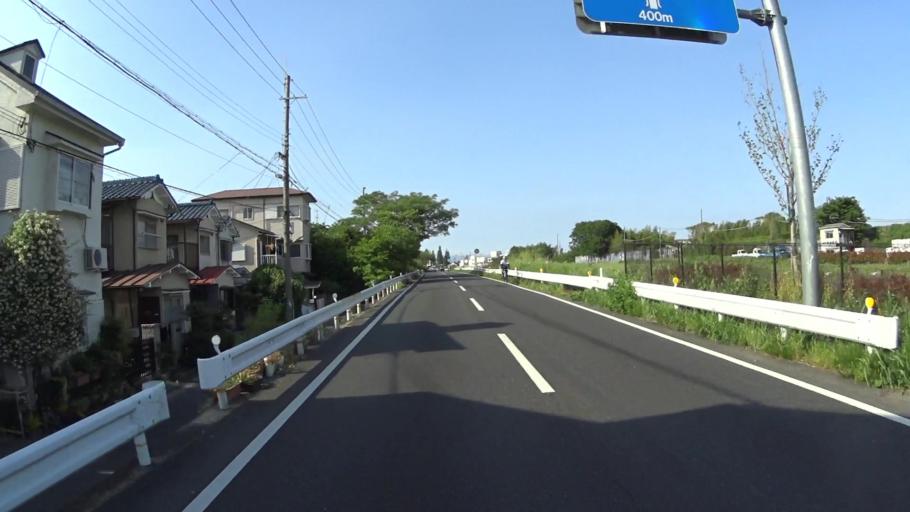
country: JP
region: Kyoto
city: Muko
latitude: 34.9306
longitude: 135.7007
